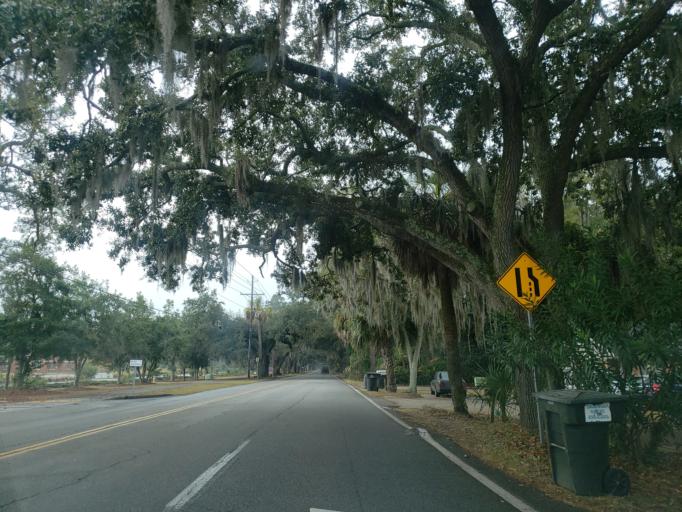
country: US
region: Georgia
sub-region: Chatham County
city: Wilmington Island
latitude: 32.0102
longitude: -80.9855
